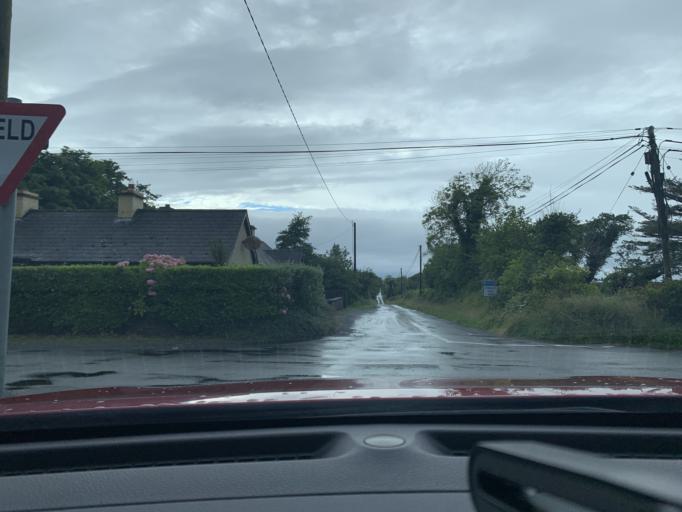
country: IE
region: Connaught
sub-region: Sligo
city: Strandhill
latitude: 54.3672
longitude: -8.5569
